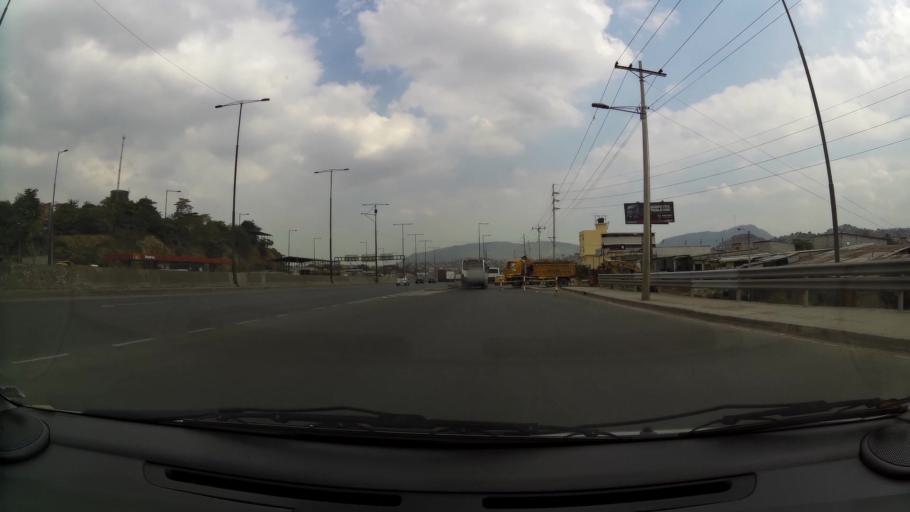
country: EC
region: Guayas
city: Santa Lucia
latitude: -2.1155
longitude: -79.9482
